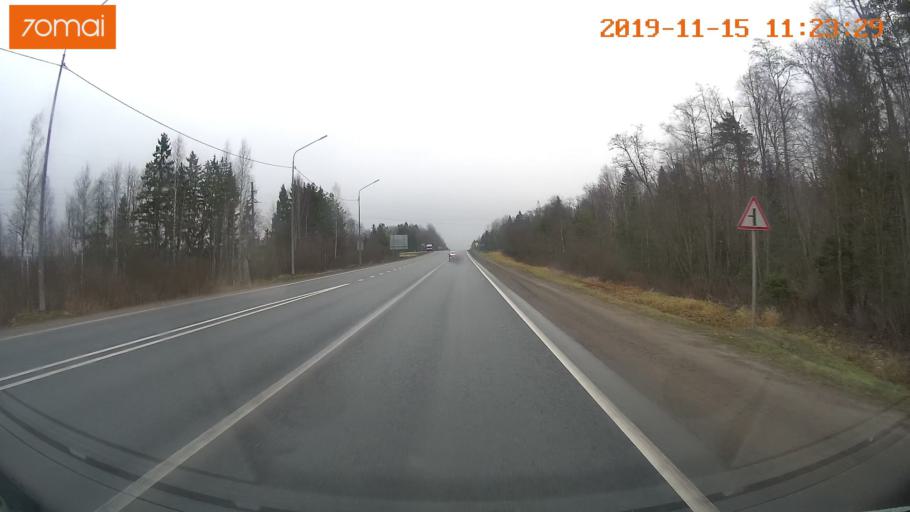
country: RU
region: Vologda
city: Molochnoye
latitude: 59.1518
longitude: 39.3832
